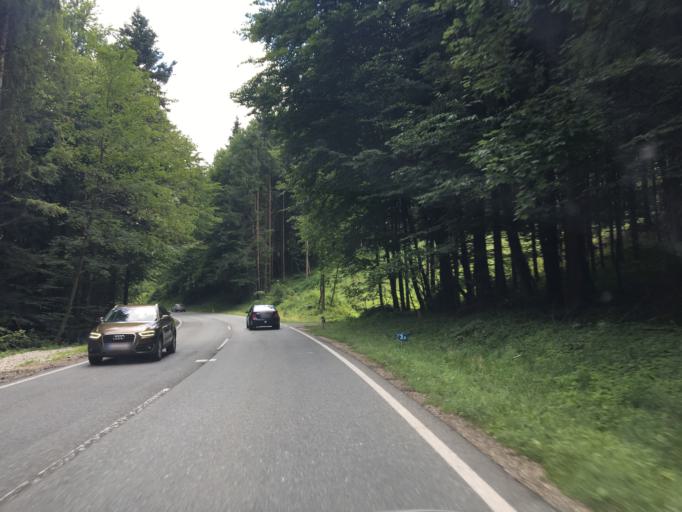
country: AT
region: Salzburg
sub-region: Politischer Bezirk Salzburg-Umgebung
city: Plainfeld
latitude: 47.8287
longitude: 13.1947
